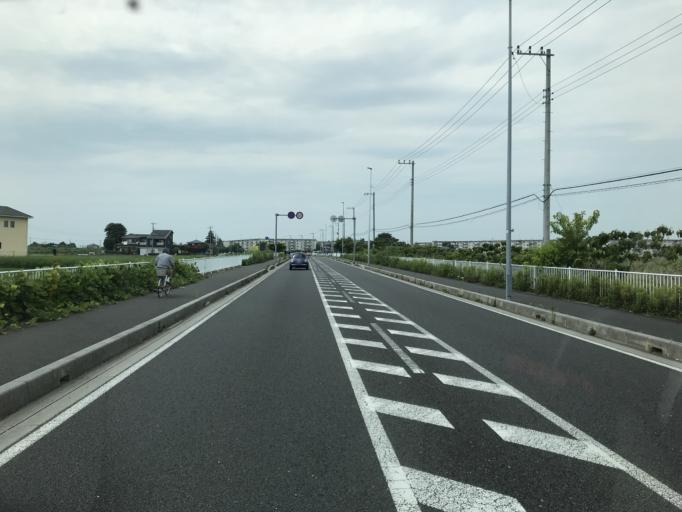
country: JP
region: Saitama
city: Kukichuo
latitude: 36.0817
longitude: 139.6625
